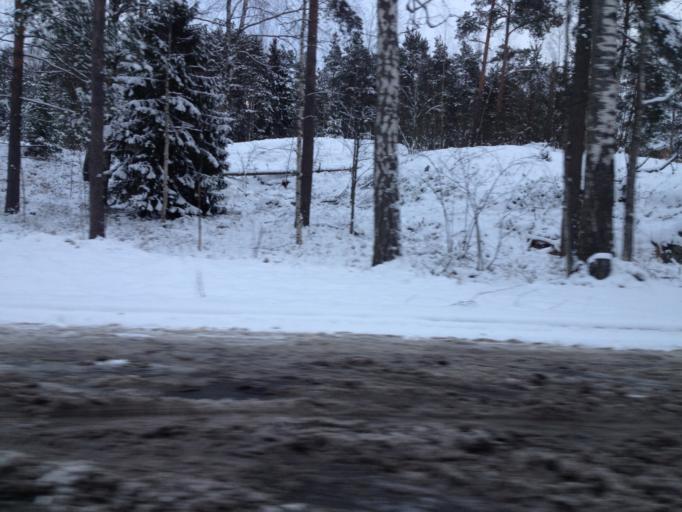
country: FI
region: Uusimaa
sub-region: Helsinki
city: Vantaa
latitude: 60.2154
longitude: 25.0446
